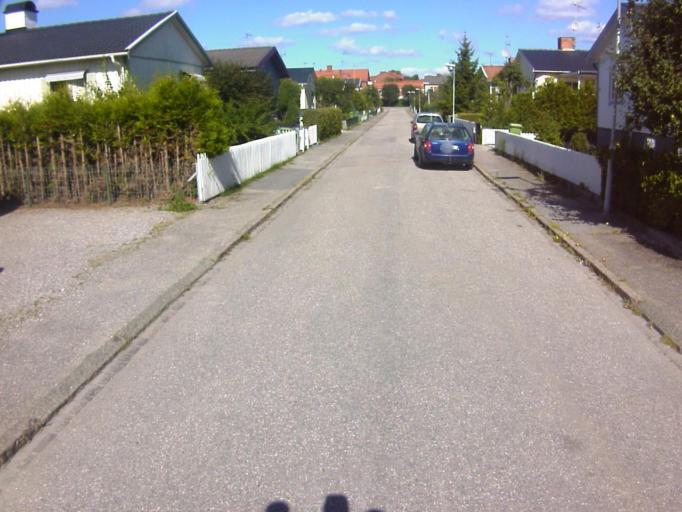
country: SE
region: Soedermanland
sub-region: Eskilstuna Kommun
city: Eskilstuna
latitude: 59.3707
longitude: 16.5396
